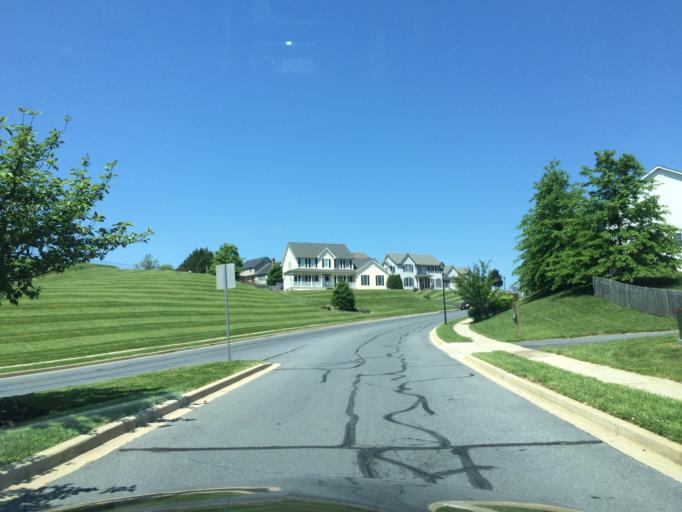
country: US
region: Maryland
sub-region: Frederick County
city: Braddock Heights
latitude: 39.4452
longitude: -77.5146
